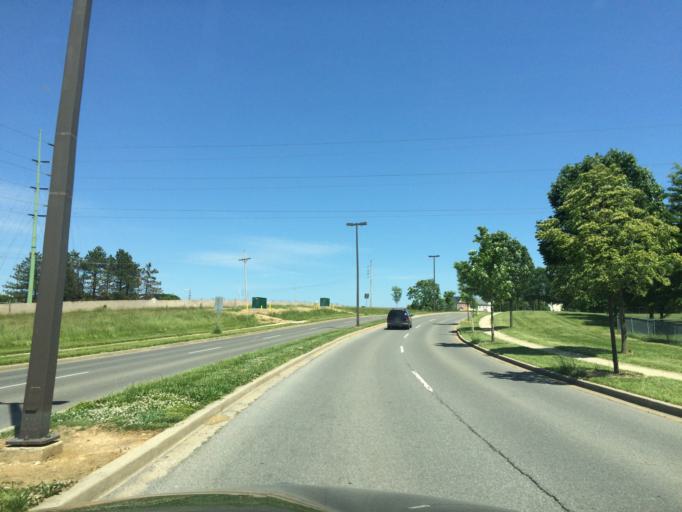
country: US
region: Maryland
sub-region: Frederick County
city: Frederick
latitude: 39.4383
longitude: -77.3960
